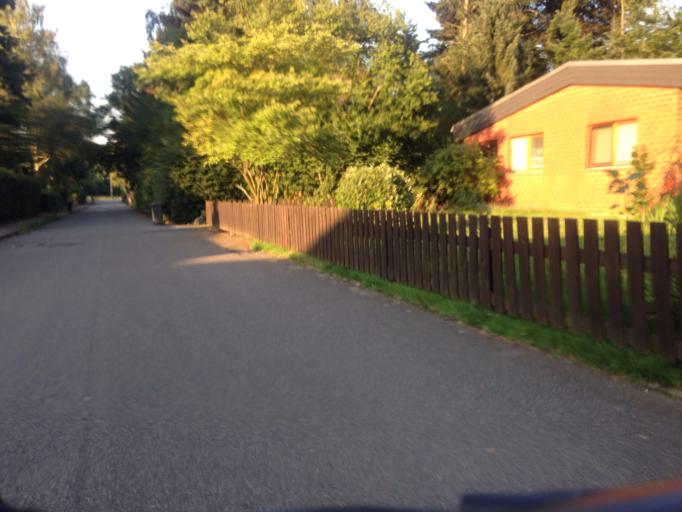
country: DE
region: Lower Saxony
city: Adendorf
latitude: 53.2803
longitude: 10.4556
